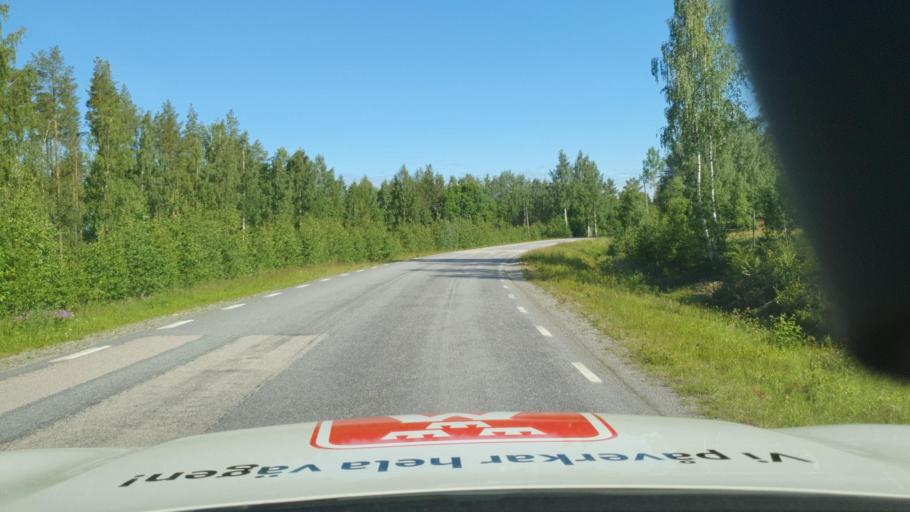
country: SE
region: Vaesterbotten
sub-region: Umea Kommun
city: Roback
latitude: 63.9262
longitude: 20.1451
